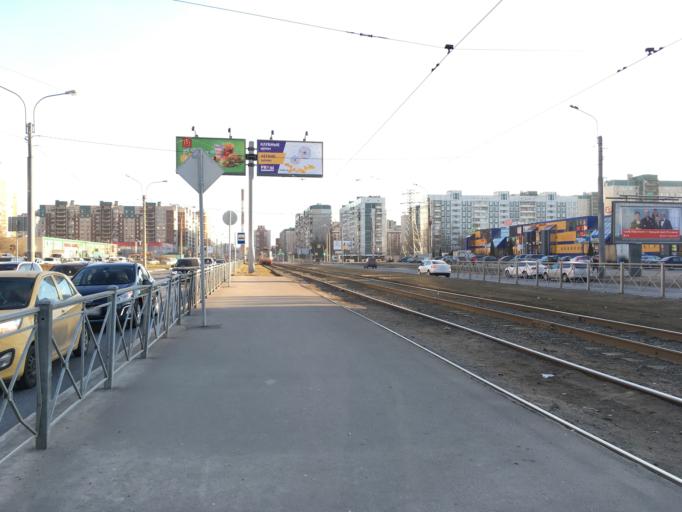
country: RU
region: St.-Petersburg
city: Staraya Derevnya
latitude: 60.0079
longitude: 30.2486
